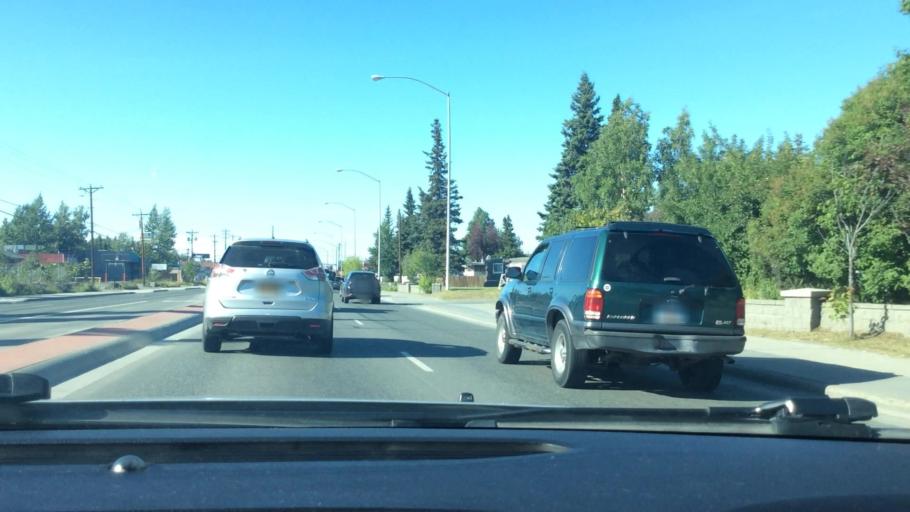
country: US
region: Alaska
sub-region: Anchorage Municipality
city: Elmendorf Air Force Base
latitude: 61.2143
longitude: -149.7334
